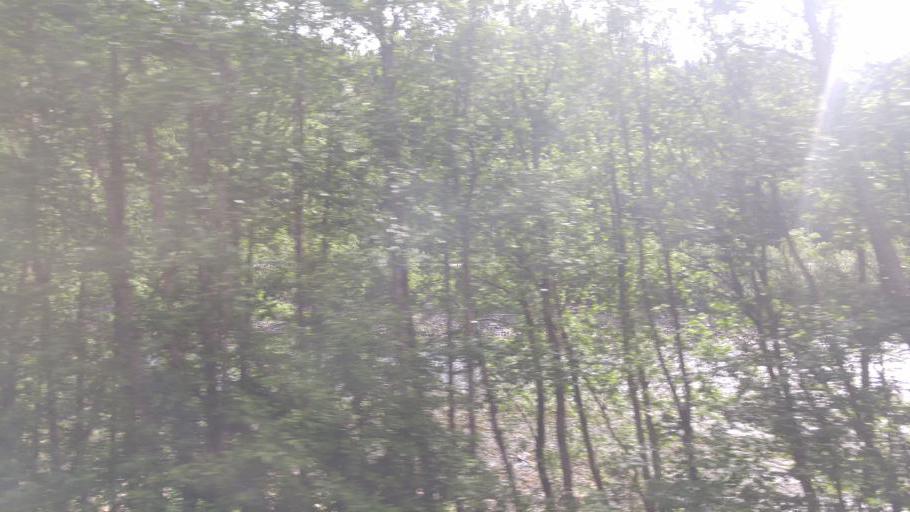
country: NO
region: Sor-Trondelag
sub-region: Midtre Gauldal
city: Storen
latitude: 63.0631
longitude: 10.2879
